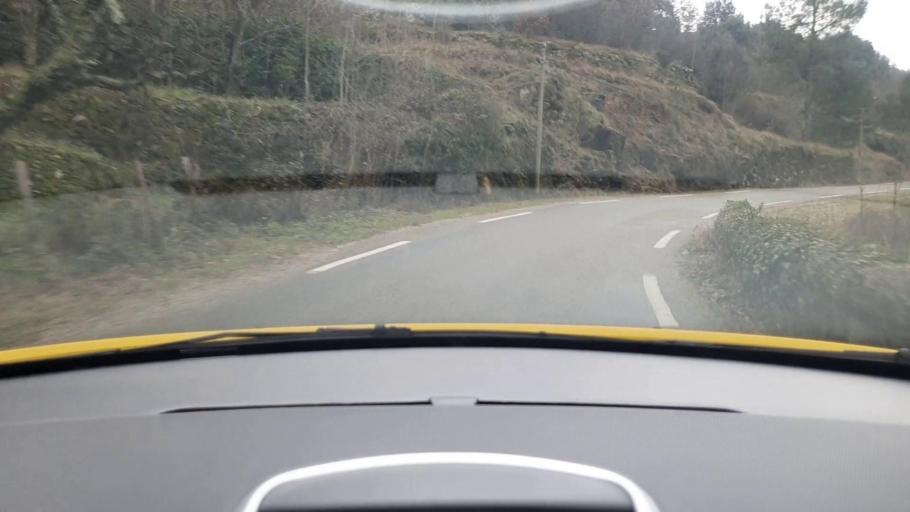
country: FR
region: Languedoc-Roussillon
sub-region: Departement du Gard
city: Besseges
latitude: 44.3431
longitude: 4.0417
